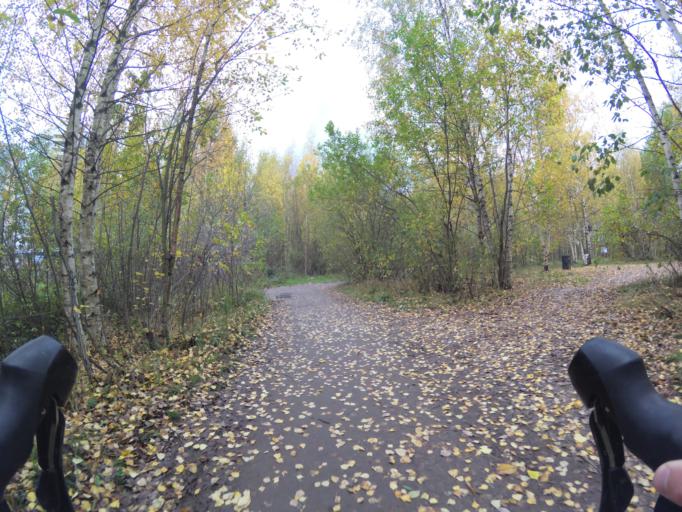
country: RU
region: Leningrad
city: Untolovo
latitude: 60.0011
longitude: 30.1930
